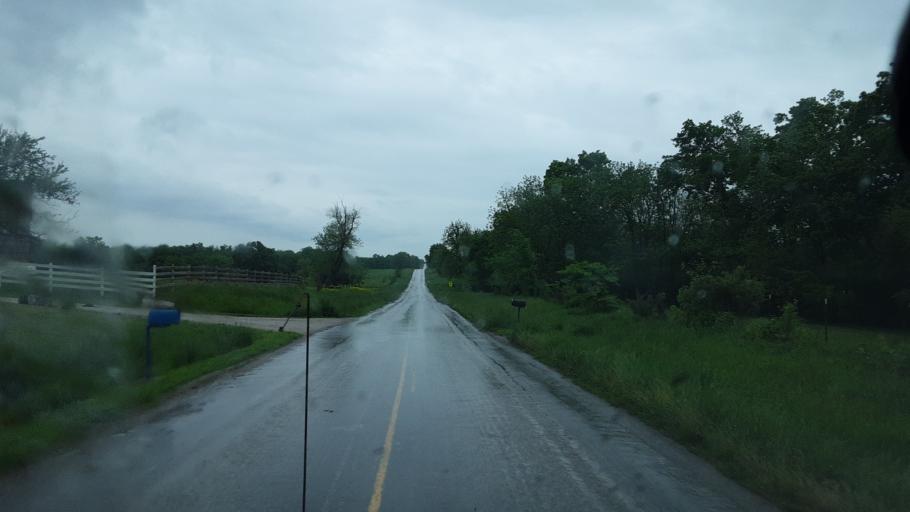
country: US
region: Missouri
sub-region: Randolph County
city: Moberly
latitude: 39.3645
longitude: -92.2680
